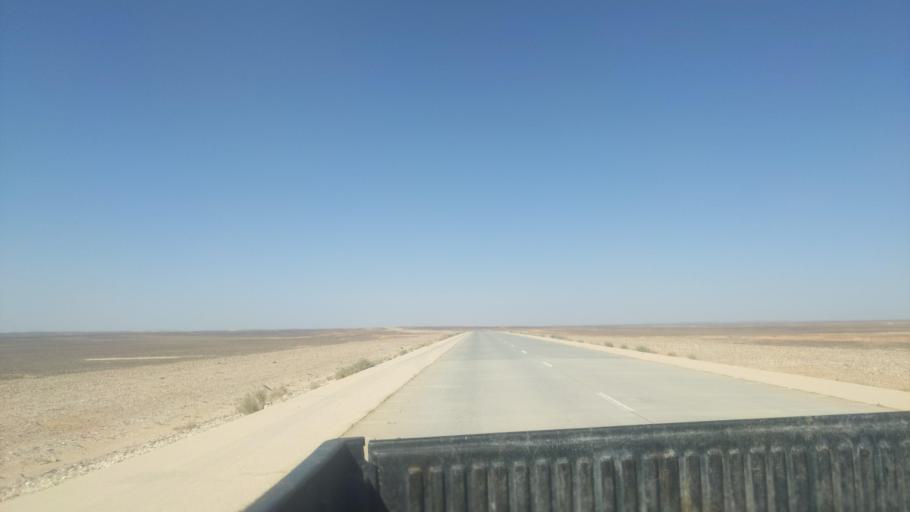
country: JO
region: Amman
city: Al Azraq ash Shamali
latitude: 31.4505
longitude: 36.7714
